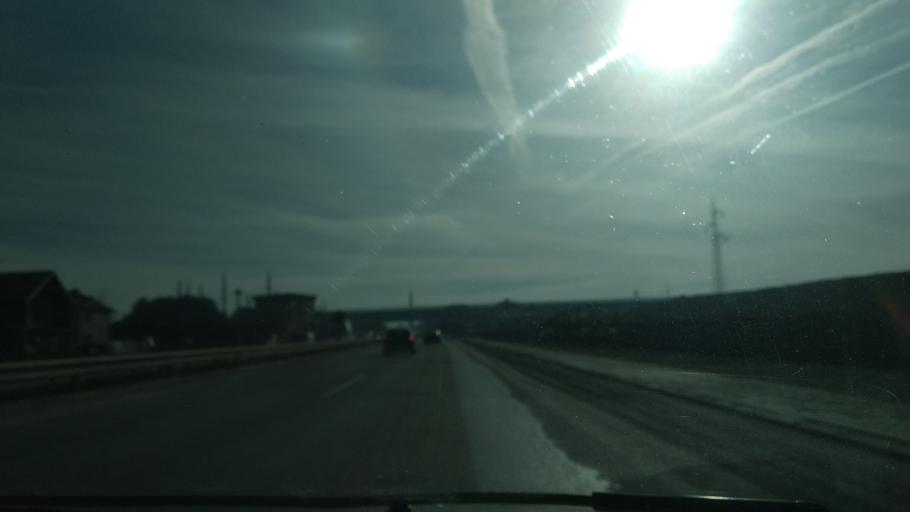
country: XK
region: Pristina
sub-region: Kosovo Polje
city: Kosovo Polje
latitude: 42.7032
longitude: 21.1084
